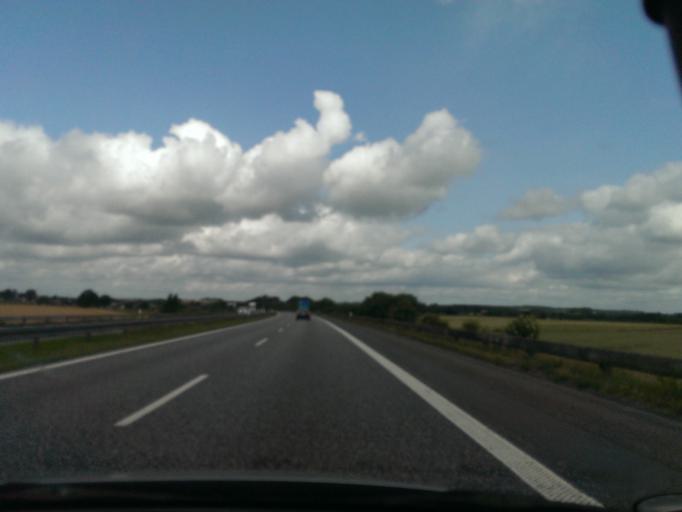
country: DK
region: Central Jutland
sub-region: Randers Kommune
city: Spentrup
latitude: 56.5339
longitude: 9.9259
